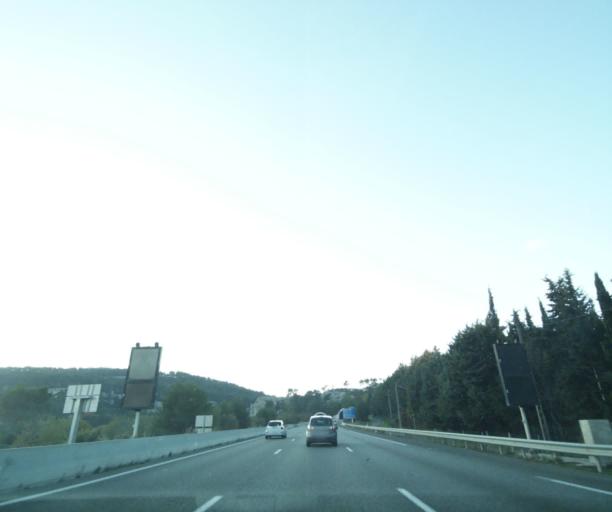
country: FR
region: Provence-Alpes-Cote d'Azur
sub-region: Departement des Bouches-du-Rhone
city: Le Tholonet
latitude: 43.5042
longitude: 5.5143
